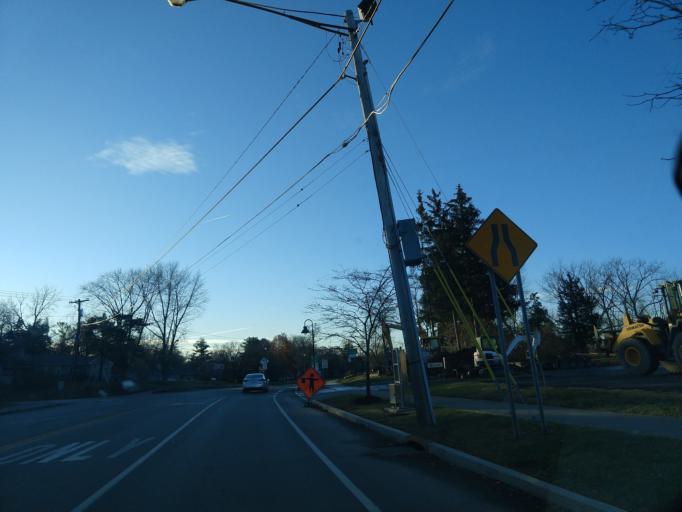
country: US
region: New York
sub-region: Tompkins County
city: Lansing
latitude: 42.4786
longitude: -76.4823
